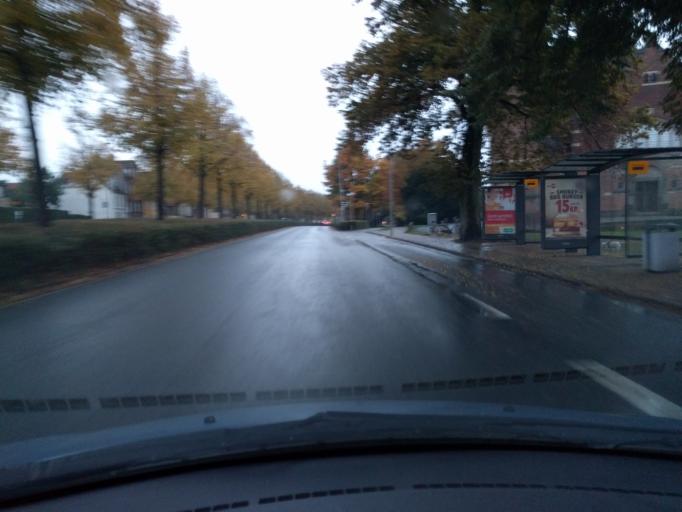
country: DK
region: South Denmark
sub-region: Odense Kommune
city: Odense
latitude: 55.3918
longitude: 10.3791
